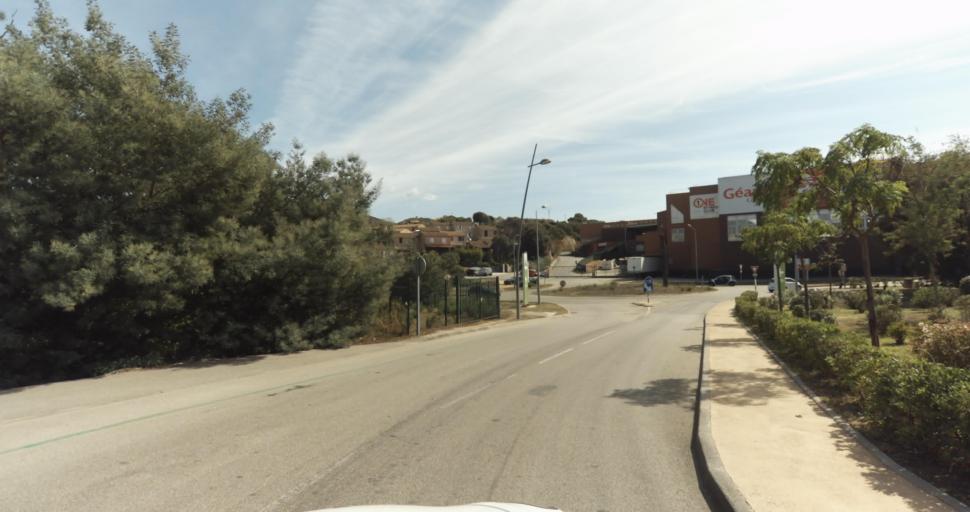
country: FR
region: Corsica
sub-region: Departement de la Corse-du-Sud
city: Afa
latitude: 41.9508
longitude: 8.7767
